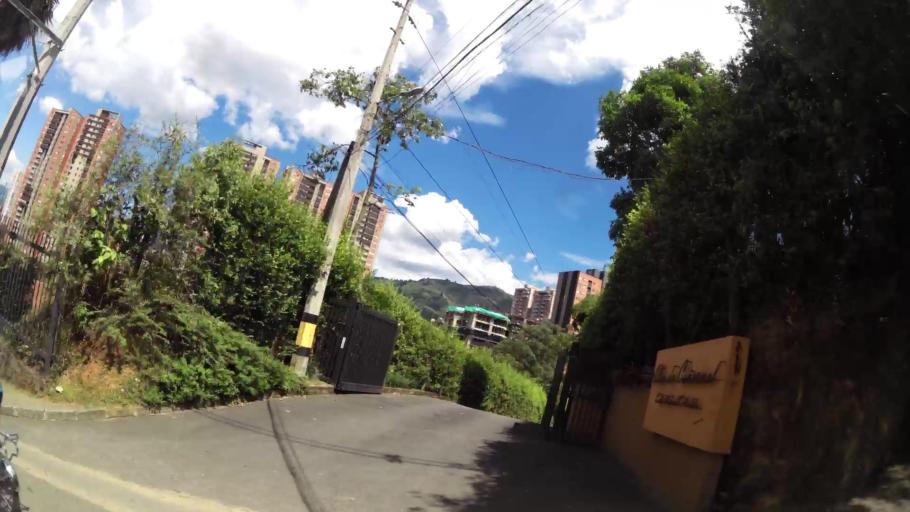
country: CO
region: Antioquia
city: Sabaneta
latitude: 6.1422
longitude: -75.6215
